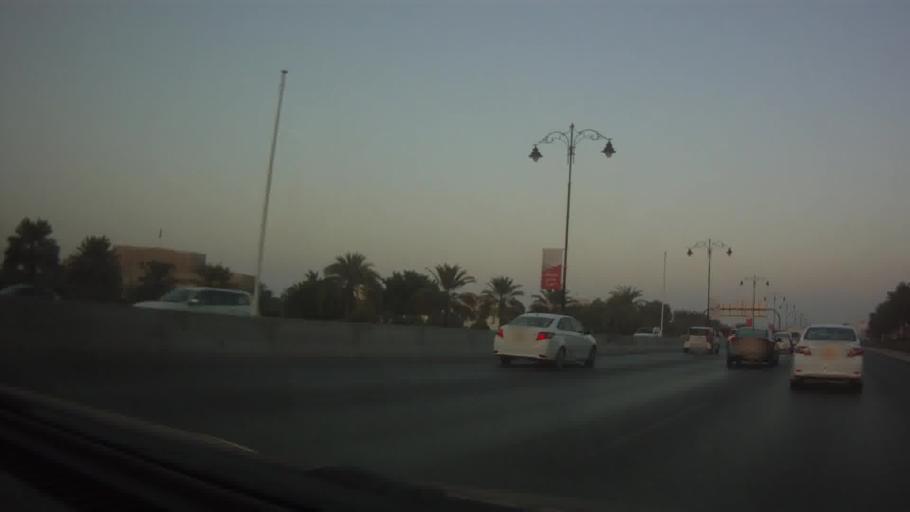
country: OM
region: Muhafazat Masqat
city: Bawshar
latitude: 23.5970
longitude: 58.4242
